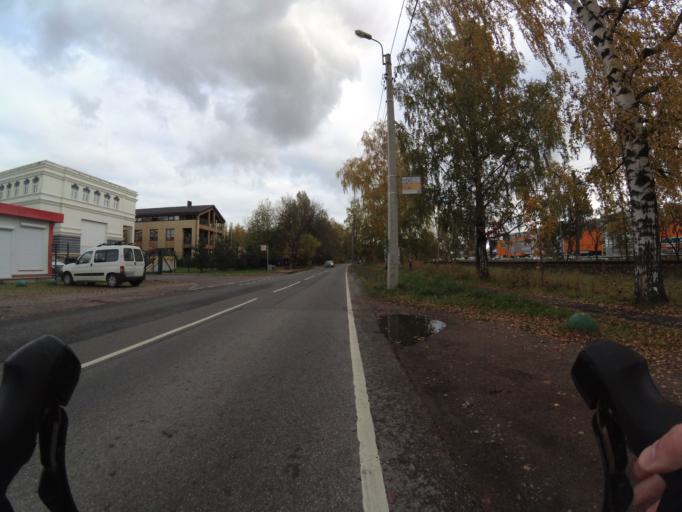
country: RU
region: St.-Petersburg
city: Lakhtinskiy
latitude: 59.9957
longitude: 30.1452
